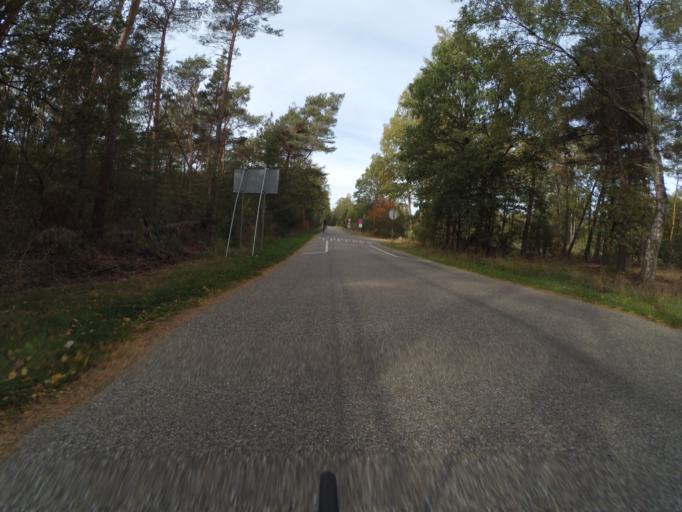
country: NL
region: Overijssel
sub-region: Gemeente Hof van Twente
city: Markelo
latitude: 52.3054
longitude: 6.4187
